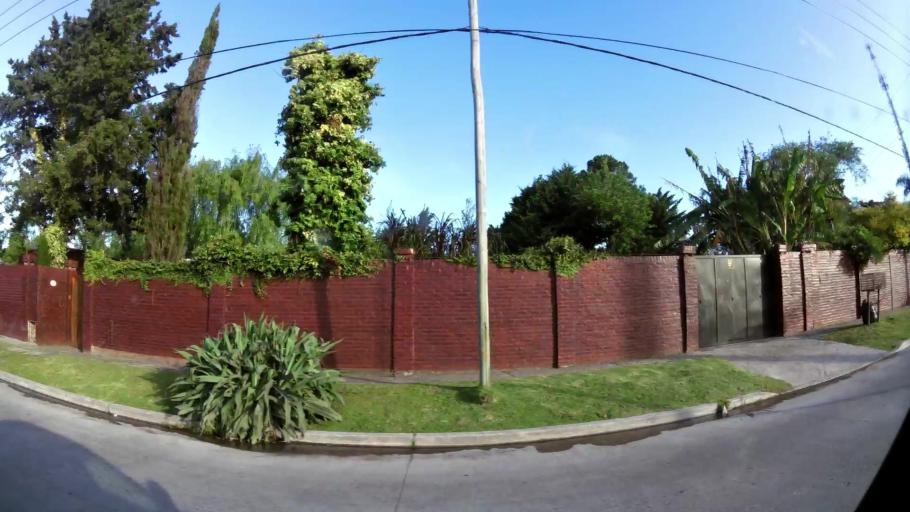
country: AR
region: Buenos Aires
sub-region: Partido de Quilmes
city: Quilmes
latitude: -34.8054
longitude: -58.2062
